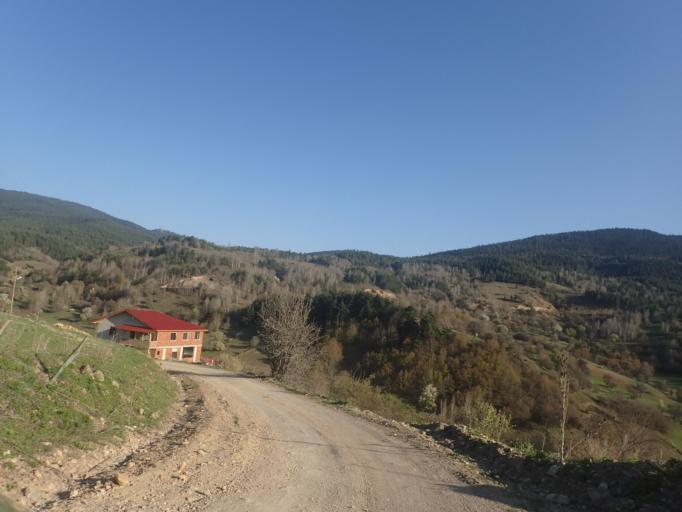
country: TR
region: Sivas
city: Koyulhisar
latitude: 40.3669
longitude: 37.8581
